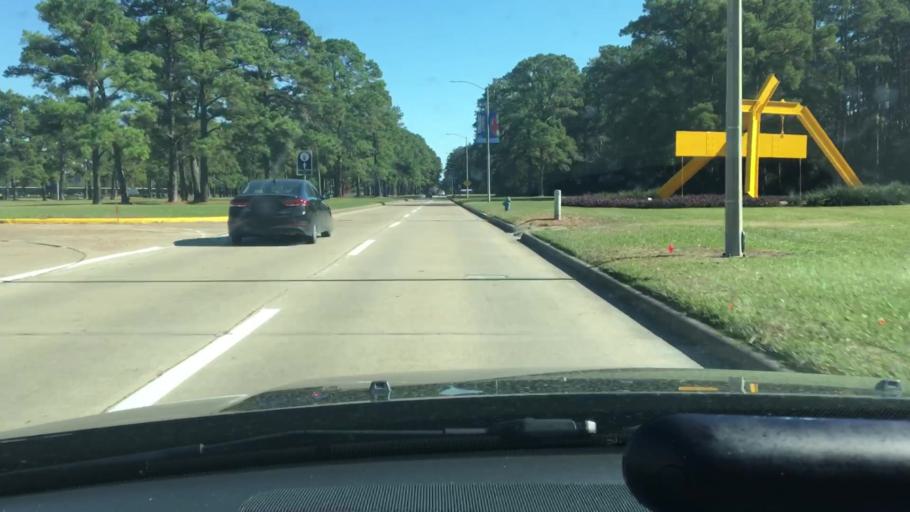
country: US
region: Texas
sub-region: Harris County
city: Humble
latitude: 29.9848
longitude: -95.3188
